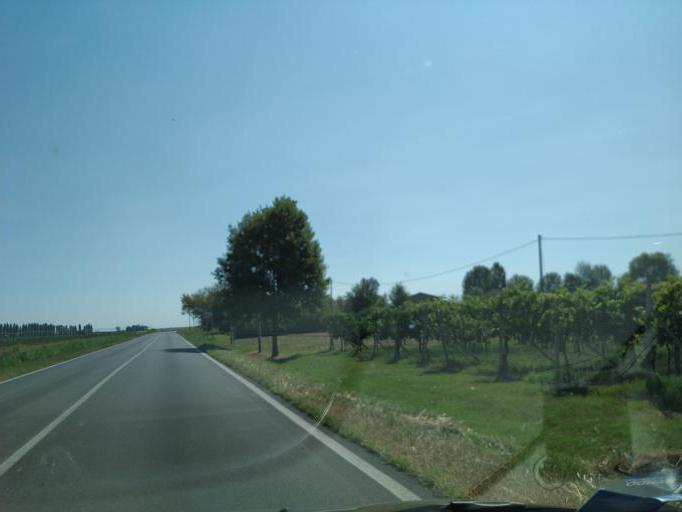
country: IT
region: Emilia-Romagna
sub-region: Provincia di Ferrara
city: Coccanile-Cesta
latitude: 44.8844
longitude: 11.8716
